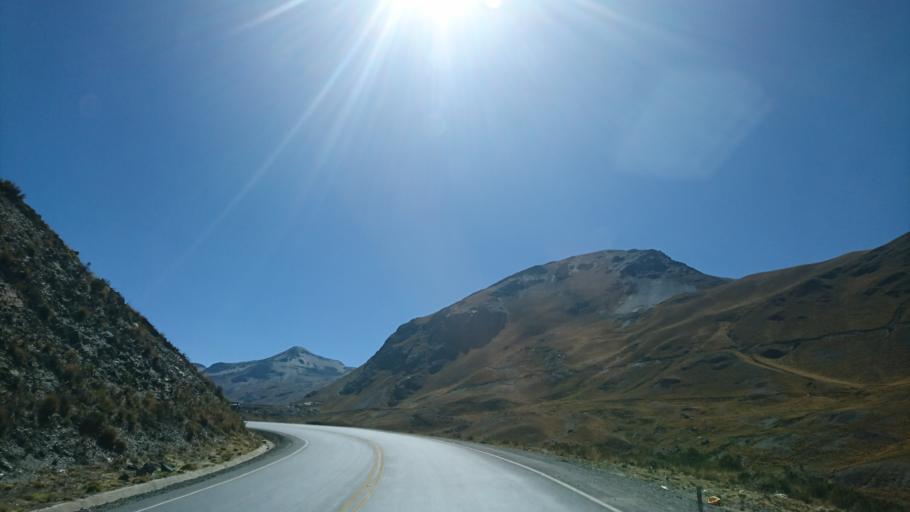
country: BO
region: La Paz
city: La Paz
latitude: -16.4165
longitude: -68.0538
